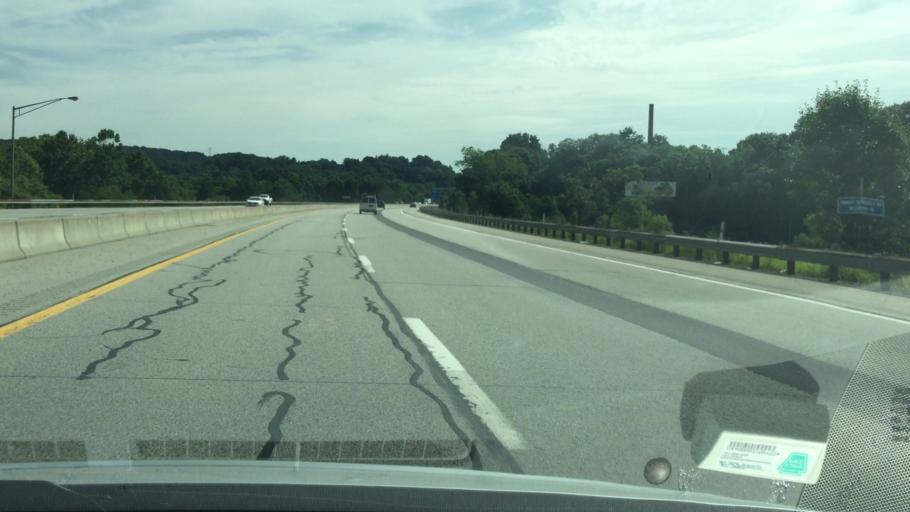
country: US
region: Pennsylvania
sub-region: Allegheny County
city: Oakmont
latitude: 40.5453
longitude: -79.8348
